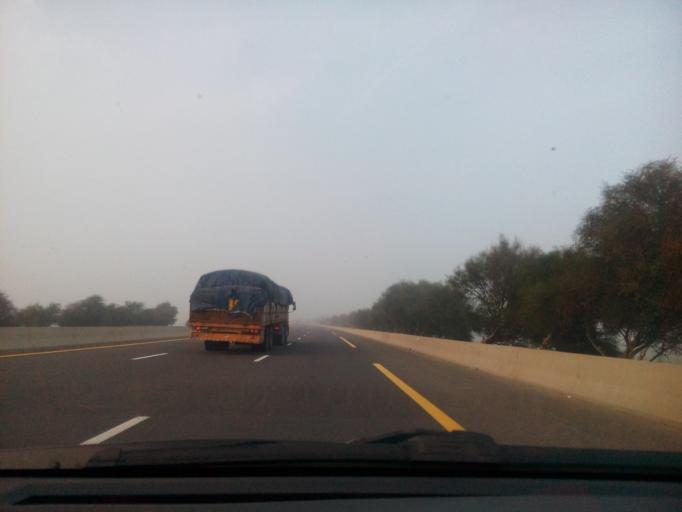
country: DZ
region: Relizane
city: Relizane
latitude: 35.7983
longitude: 0.5098
